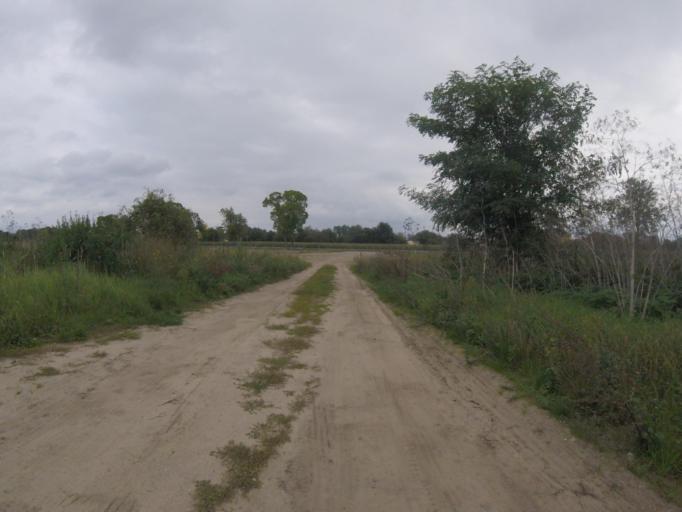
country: DE
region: Brandenburg
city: Mittenwalde
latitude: 52.2539
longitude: 13.5160
